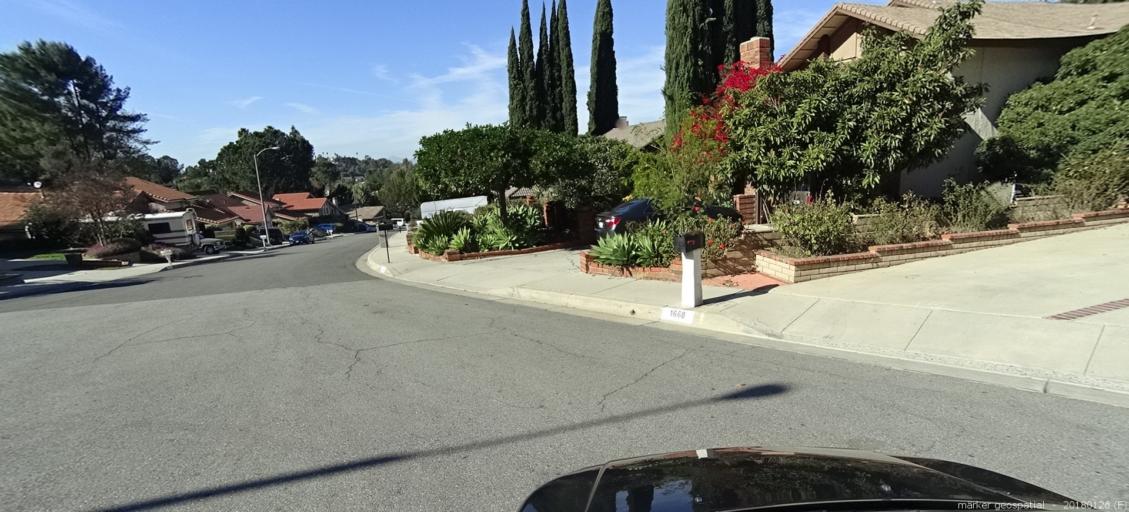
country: US
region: California
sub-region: Los Angeles County
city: Diamond Bar
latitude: 33.9919
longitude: -117.8074
